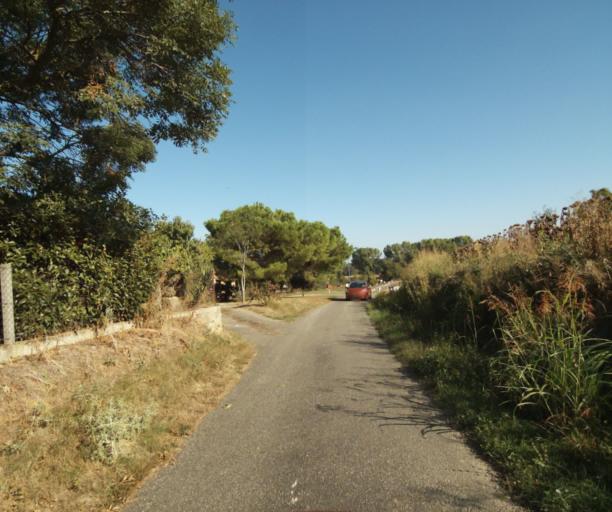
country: FR
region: Midi-Pyrenees
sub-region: Departement du Tarn-et-Garonne
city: Verdun-sur-Garonne
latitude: 43.8580
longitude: 1.2306
